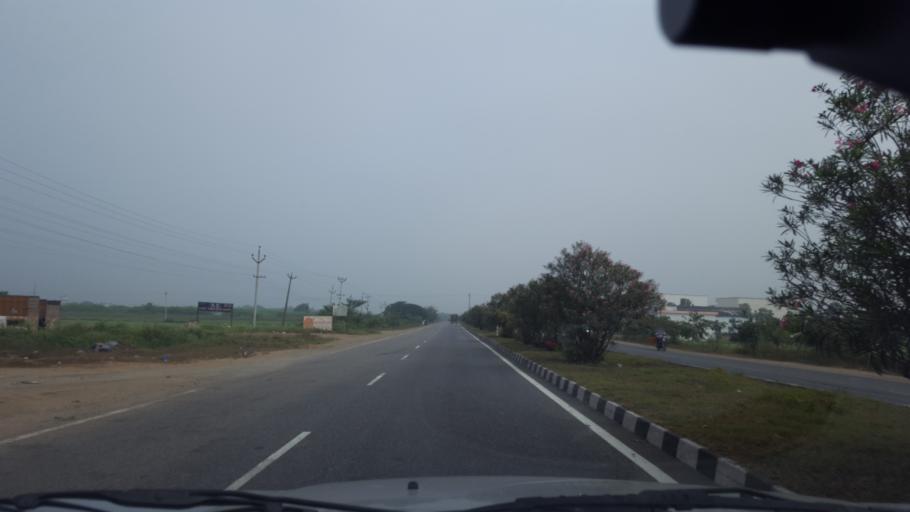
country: IN
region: Andhra Pradesh
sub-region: Guntur
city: Chilakalurupet
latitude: 16.0647
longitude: 80.1505
